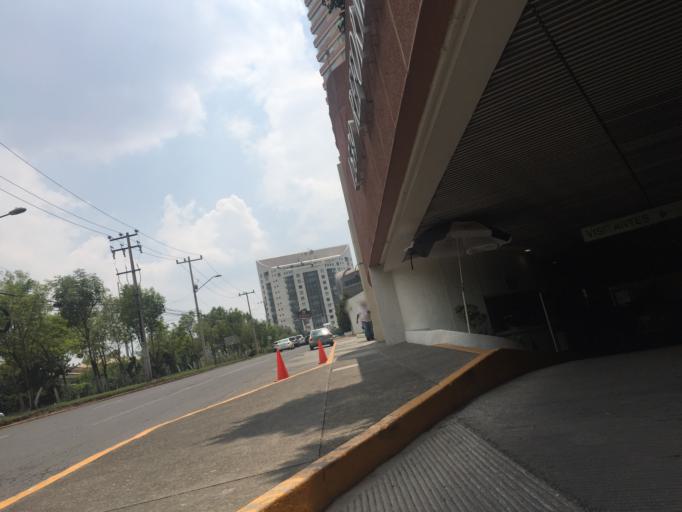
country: MX
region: Mexico City
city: Col. Bosques de las Lomas
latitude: 19.3847
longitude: -99.2648
